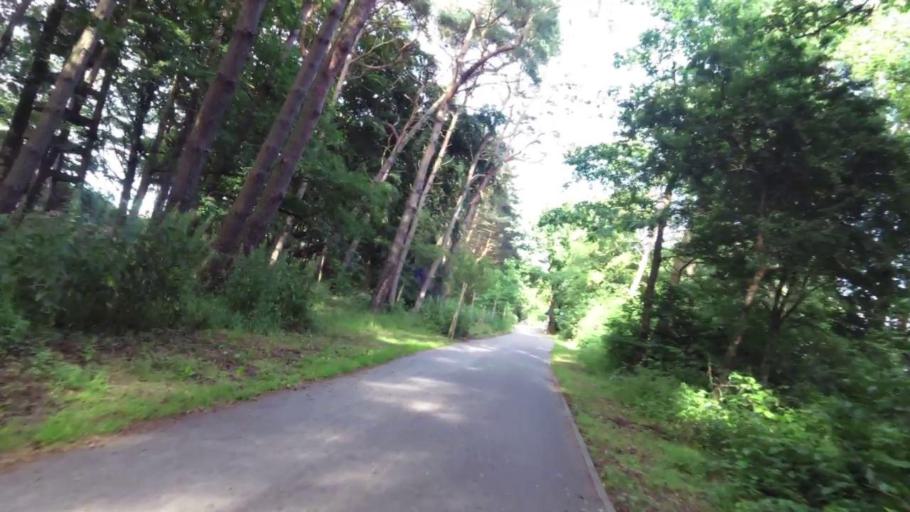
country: PL
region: West Pomeranian Voivodeship
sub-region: Powiat kolobrzeski
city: Grzybowo
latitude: 54.1663
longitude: 15.4905
